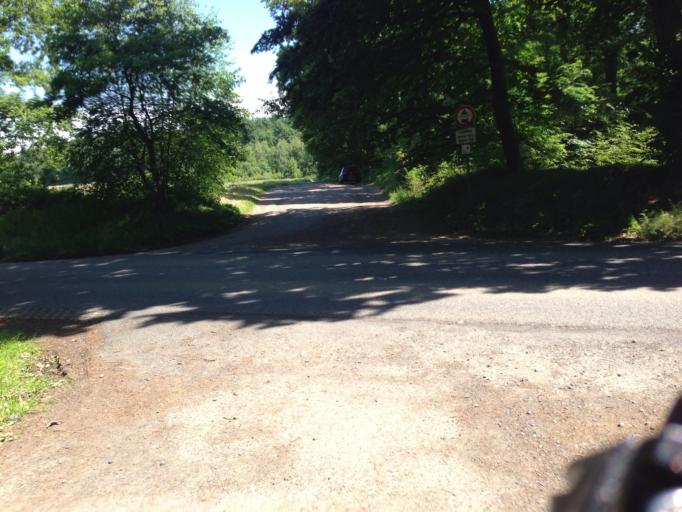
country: DE
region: Hesse
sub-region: Regierungsbezirk Darmstadt
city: Hammersbach
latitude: 50.2456
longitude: 9.0361
